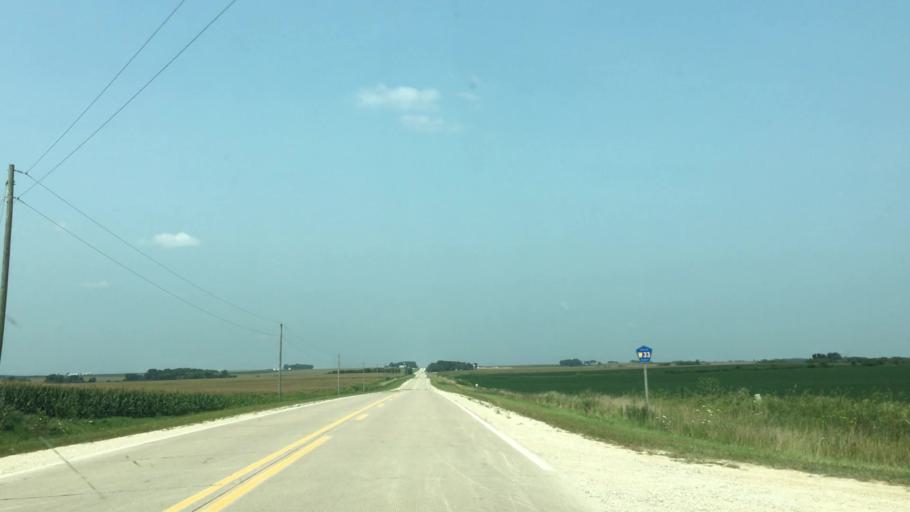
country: US
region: Iowa
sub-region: Fayette County
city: Fayette
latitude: 42.7453
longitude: -91.8041
